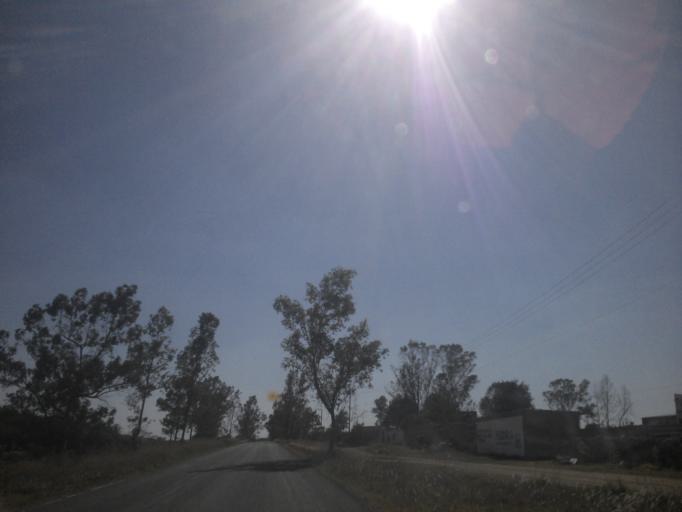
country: MX
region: Jalisco
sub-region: Arandas
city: Santiaguito (Santiaguito de Velazquez)
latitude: 20.8310
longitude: -102.1228
